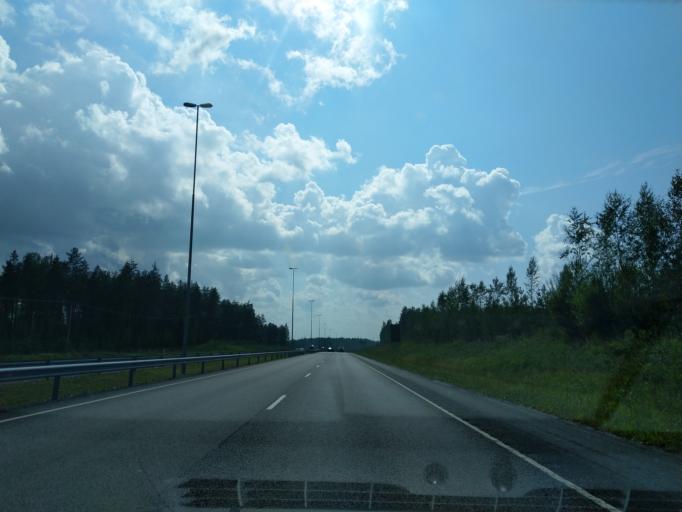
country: FI
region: South Karelia
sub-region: Lappeenranta
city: Joutseno
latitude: 61.0894
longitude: 28.3592
